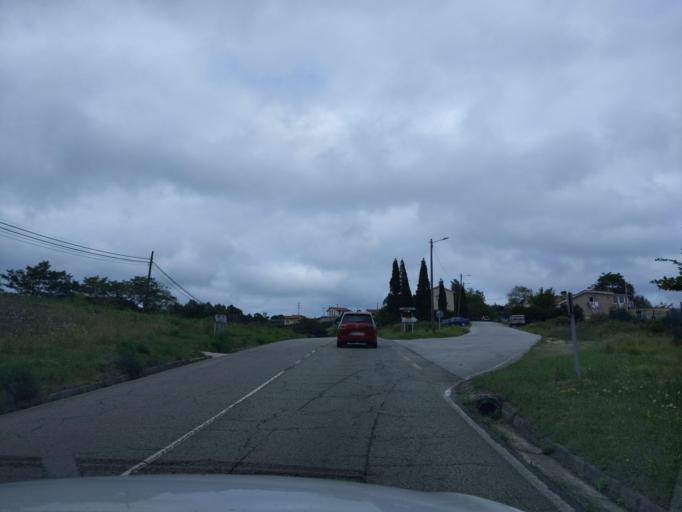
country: ES
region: Asturias
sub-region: Province of Asturias
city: Aviles
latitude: 43.5850
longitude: -5.9140
